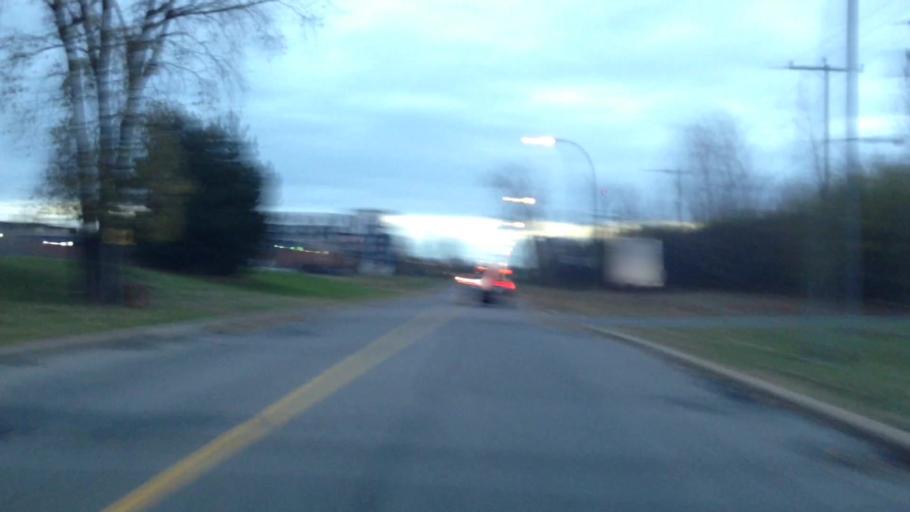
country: CA
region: Quebec
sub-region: Montreal
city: Pointe-Claire
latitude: 45.4561
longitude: -73.8393
